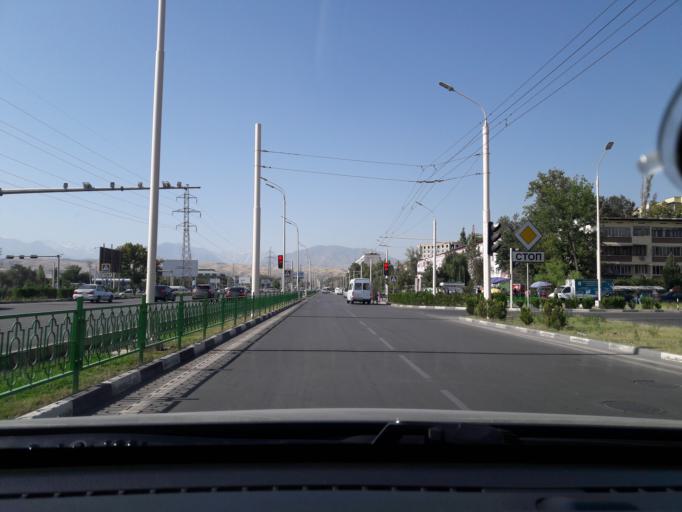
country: TJ
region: Dushanbe
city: Dushanbe
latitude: 38.5498
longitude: 68.7415
